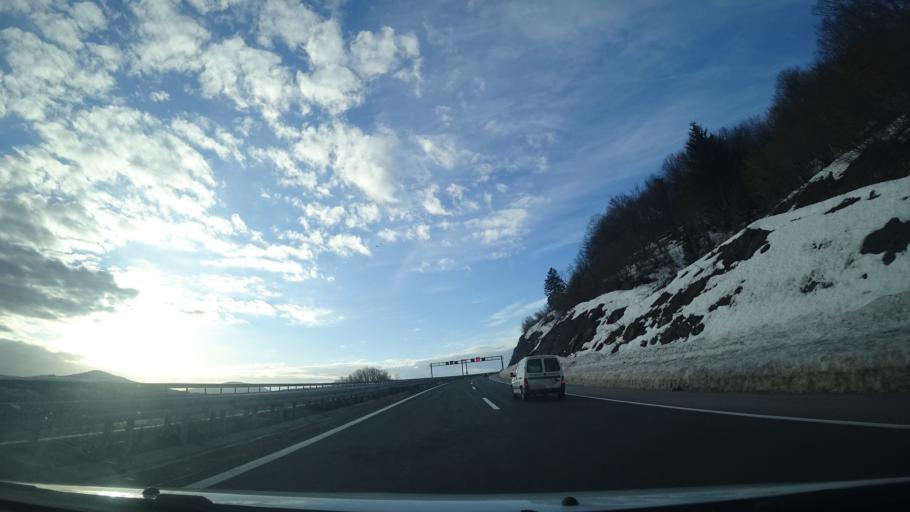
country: HR
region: Karlovacka
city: Ostarije
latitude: 45.1782
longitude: 15.2764
